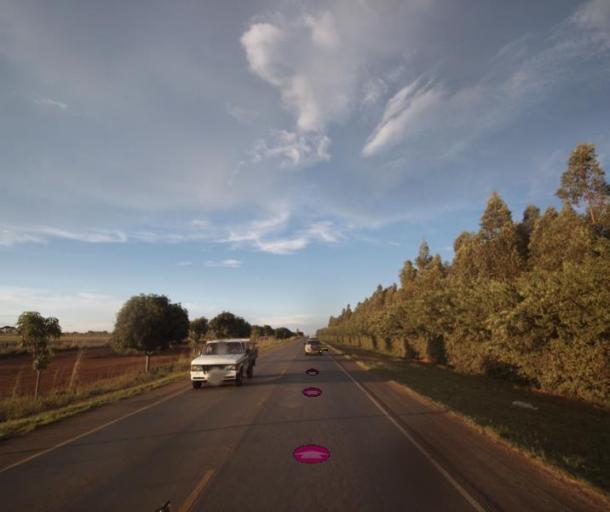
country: BR
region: Goias
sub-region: Anapolis
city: Anapolis
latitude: -16.2138
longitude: -48.9182
